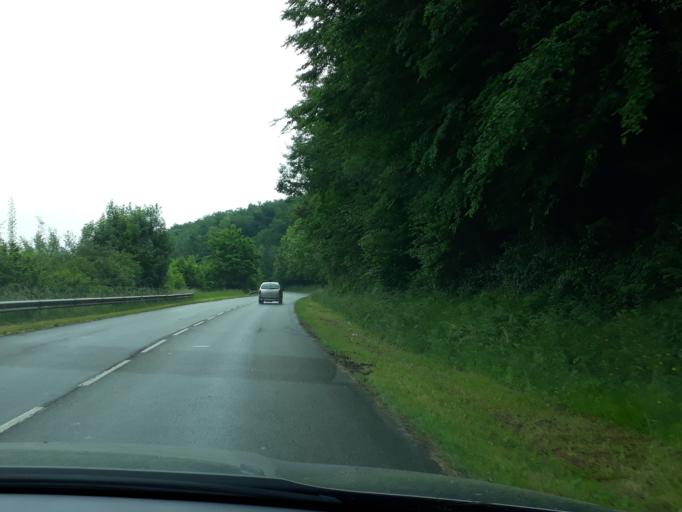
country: FR
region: Limousin
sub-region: Departement de la Correze
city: Cosnac
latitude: 45.1536
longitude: 1.6200
